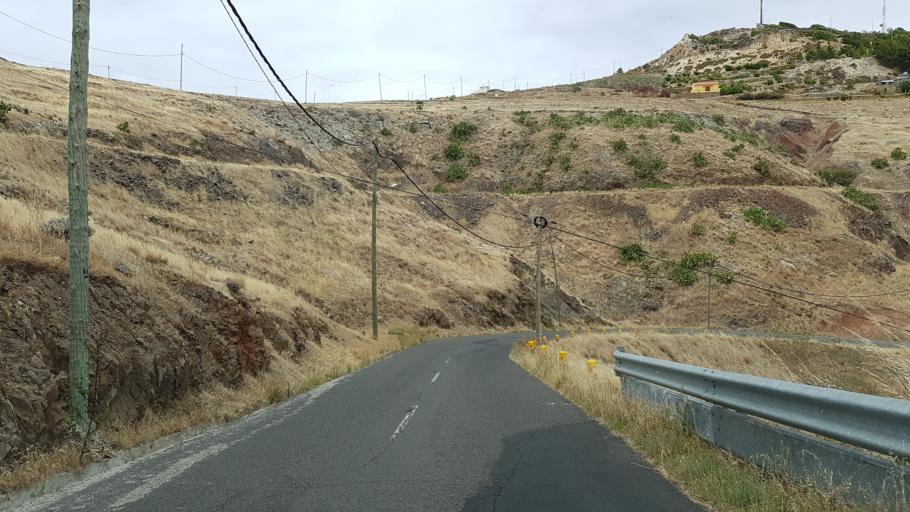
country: PT
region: Madeira
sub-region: Porto Santo
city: Vila de Porto Santo
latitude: 33.0705
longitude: -16.3138
